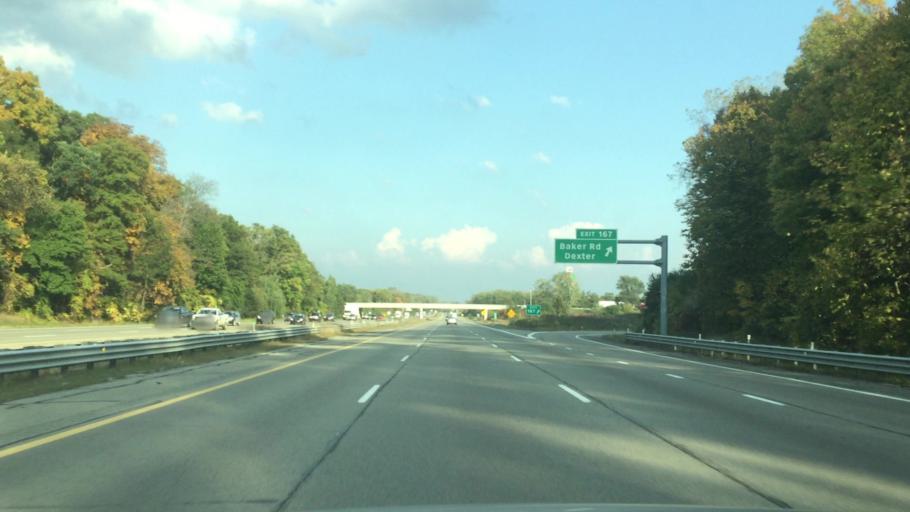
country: US
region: Michigan
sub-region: Washtenaw County
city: Dexter
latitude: 42.2982
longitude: -83.8834
